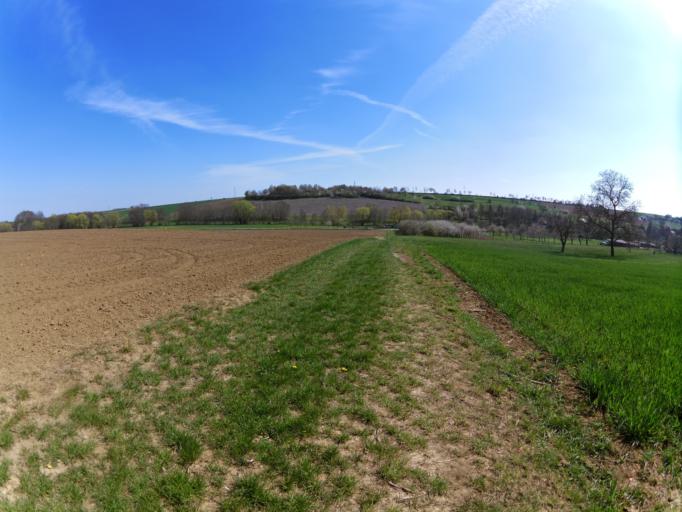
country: DE
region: Bavaria
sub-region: Regierungsbezirk Unterfranken
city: Kurnach
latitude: 49.8601
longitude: 10.0152
